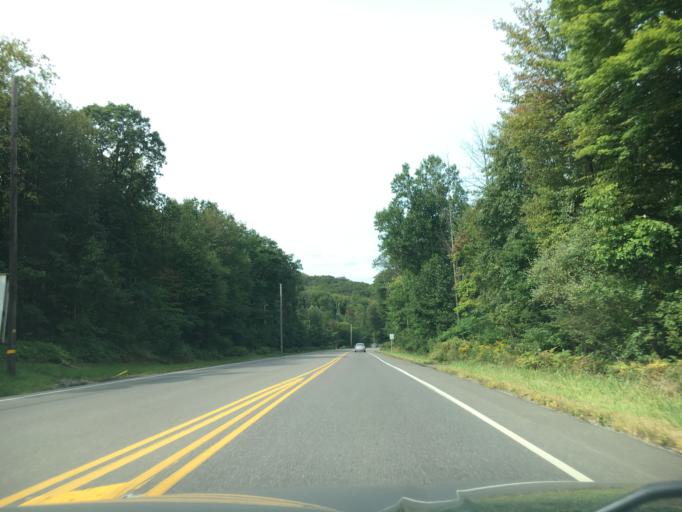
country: US
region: Pennsylvania
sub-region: Carbon County
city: Summit Hill
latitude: 40.7073
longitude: -75.8110
